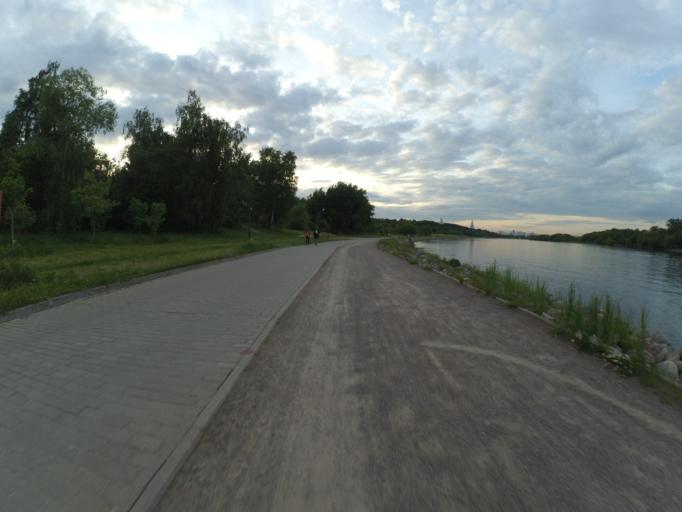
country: RU
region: Moscow
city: Kolomenskoye
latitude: 55.6541
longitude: 37.6702
